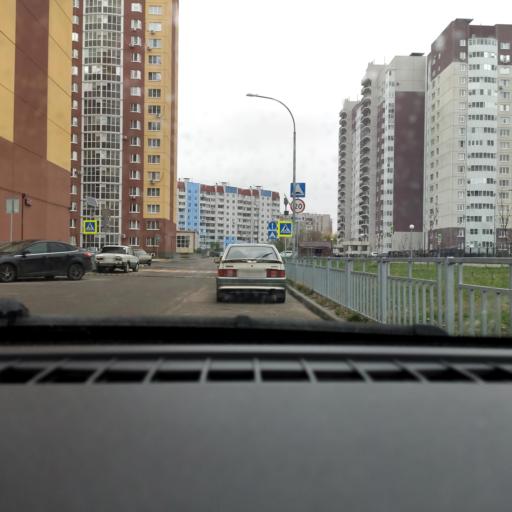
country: RU
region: Voronezj
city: Voronezh
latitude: 51.7158
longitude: 39.2656
